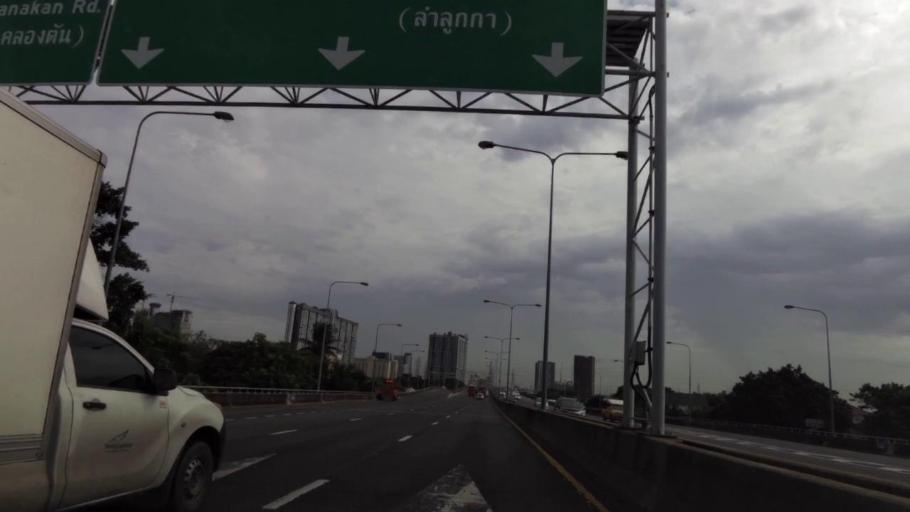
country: TH
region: Bangkok
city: Watthana
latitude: 13.7340
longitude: 100.6042
